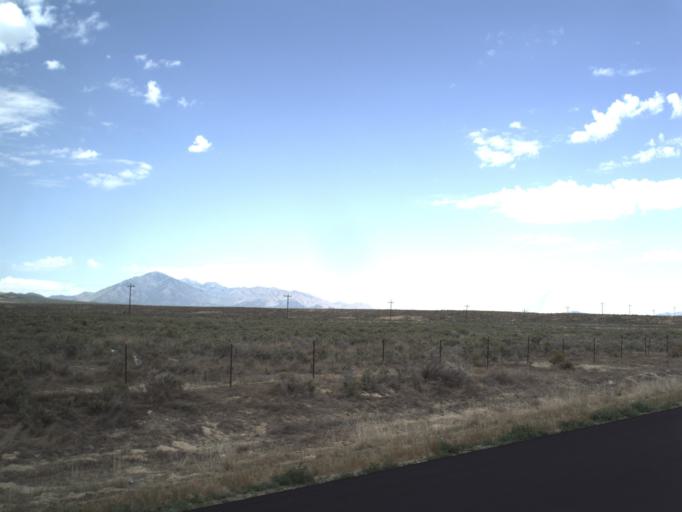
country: US
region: Utah
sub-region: Tooele County
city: Tooele
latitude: 40.1739
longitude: -112.4273
